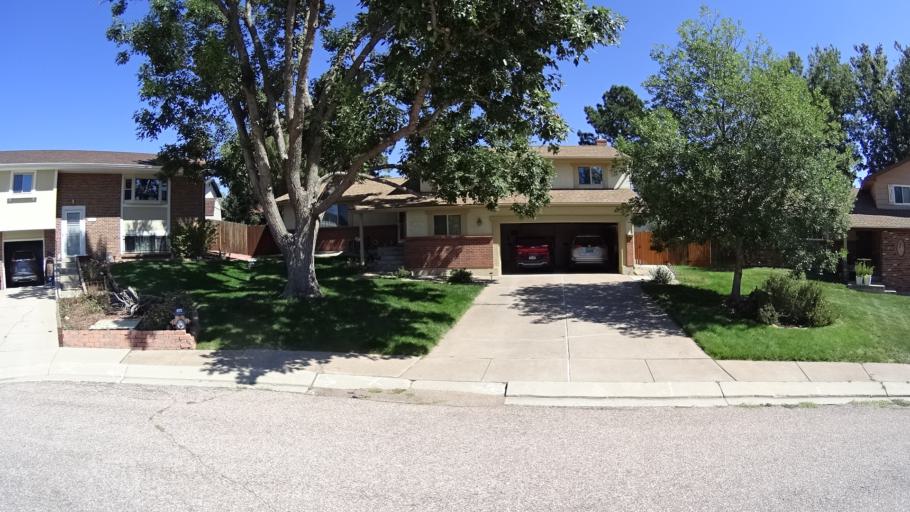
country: US
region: Colorado
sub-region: El Paso County
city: Cimarron Hills
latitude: 38.8684
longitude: -104.7284
